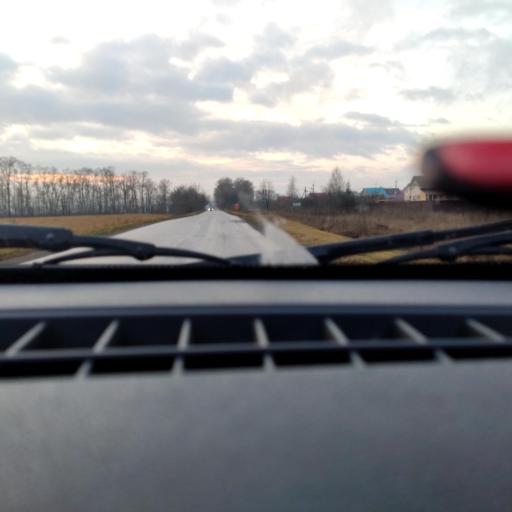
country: RU
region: Bashkortostan
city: Avdon
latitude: 54.5092
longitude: 55.8352
